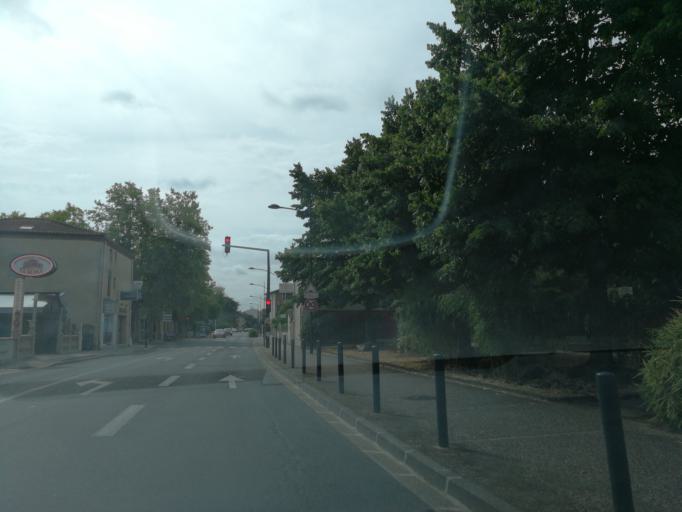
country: FR
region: Midi-Pyrenees
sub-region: Departement de la Haute-Garonne
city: Aucamville
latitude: 43.6695
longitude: 1.4284
